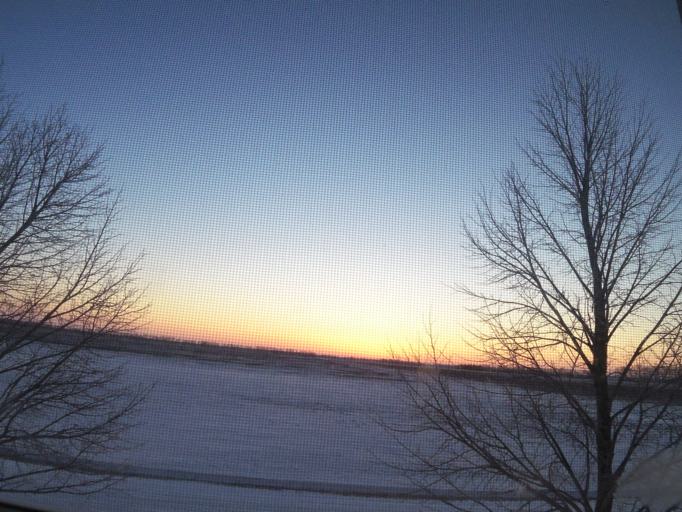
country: US
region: North Dakota
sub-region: Walsh County
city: Grafton
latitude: 48.3980
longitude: -97.2099
